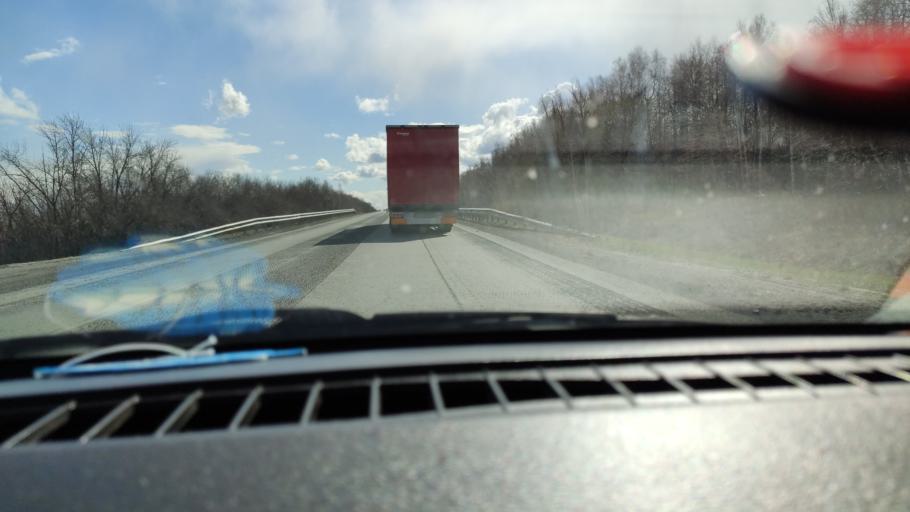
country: RU
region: Saratov
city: Dukhovnitskoye
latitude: 52.6355
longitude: 48.1876
